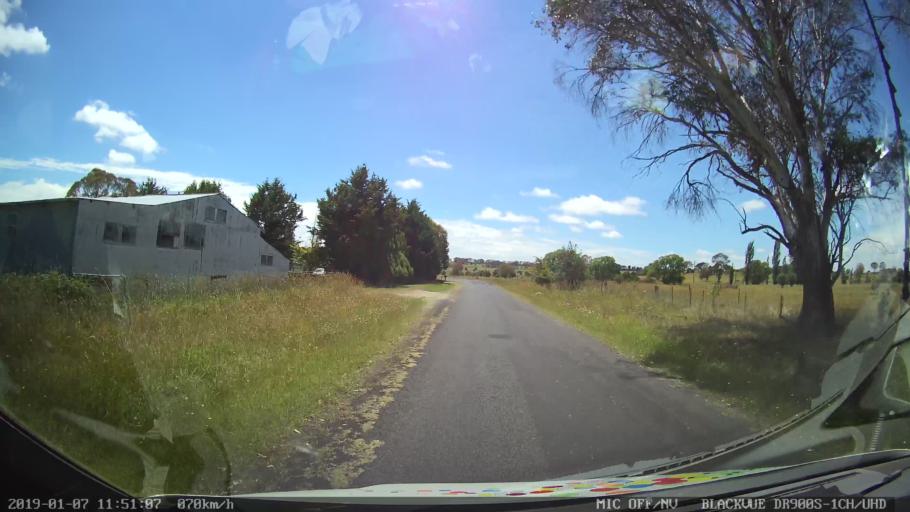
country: AU
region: New South Wales
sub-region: Guyra
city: Guyra
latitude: -30.3096
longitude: 151.6427
